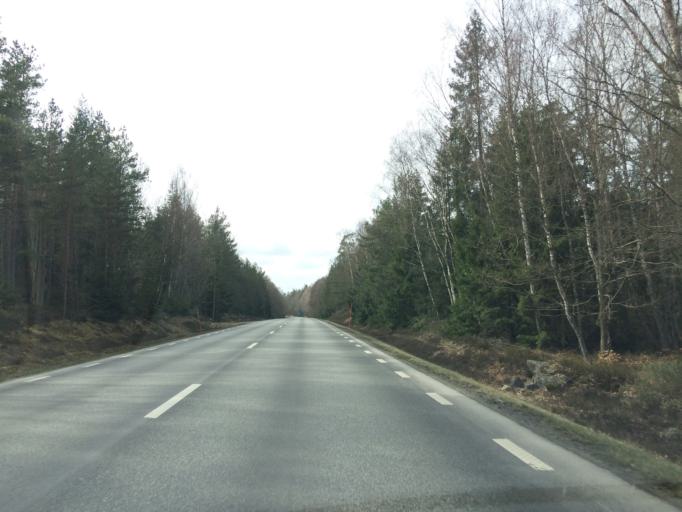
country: SE
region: Skane
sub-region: Osby Kommun
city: Lonsboda
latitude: 56.3813
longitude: 14.2655
